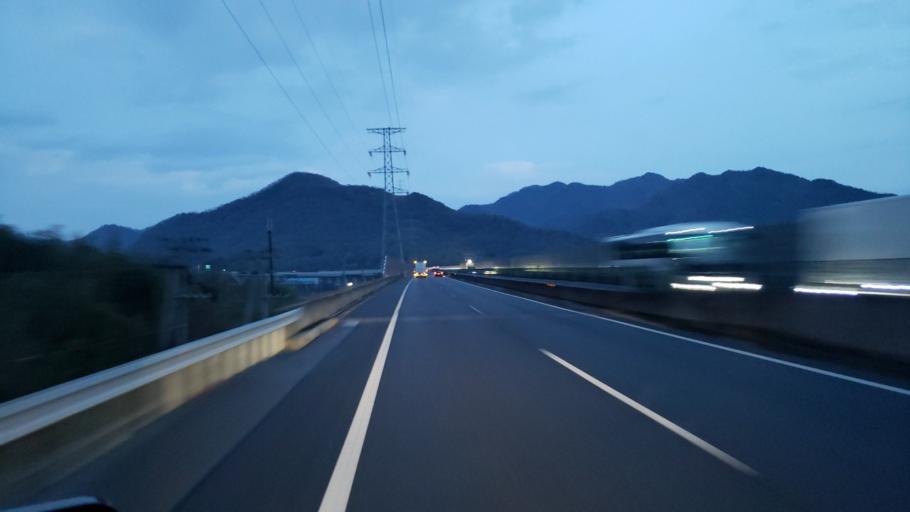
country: JP
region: Hyogo
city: Himeji
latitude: 34.8501
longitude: 134.7487
